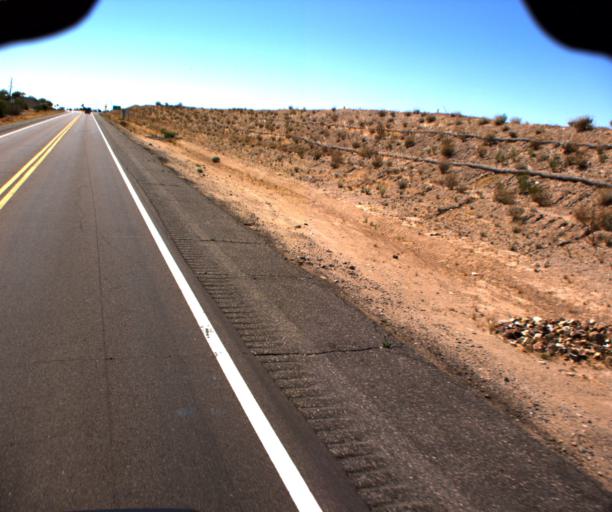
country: US
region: Arizona
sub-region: Maricopa County
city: Wickenburg
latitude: 34.0210
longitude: -112.8033
